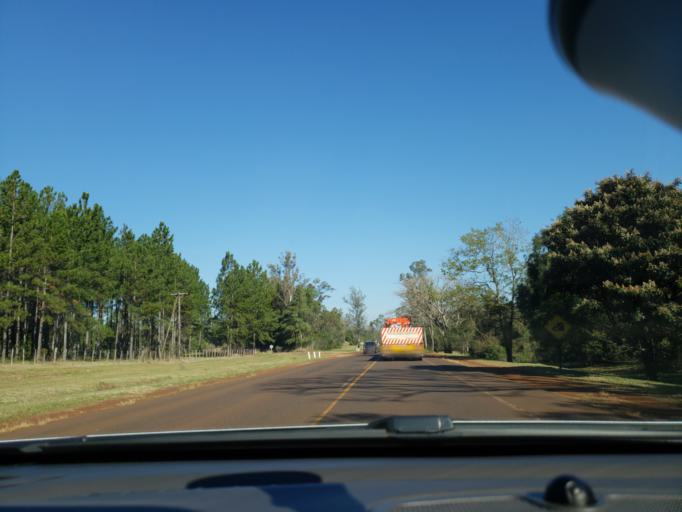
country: AR
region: Misiones
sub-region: Departamento de Apostoles
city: San Jose
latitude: -27.8144
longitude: -55.7689
